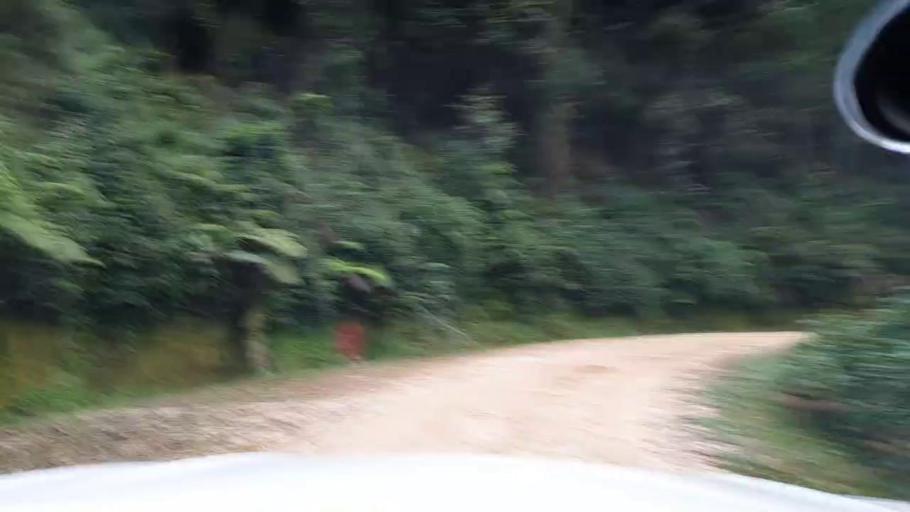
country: RW
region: Western Province
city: Cyangugu
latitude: -2.5696
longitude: 29.2261
